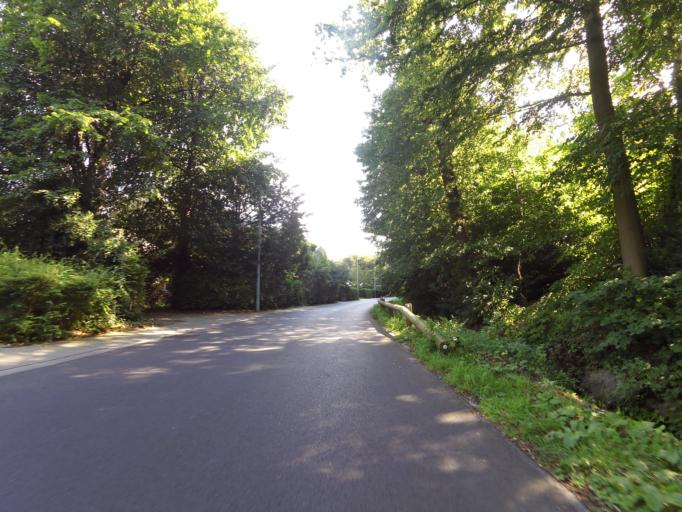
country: BE
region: Flanders
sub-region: Provincie West-Vlaanderen
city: Brugge
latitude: 51.1958
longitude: 3.1672
